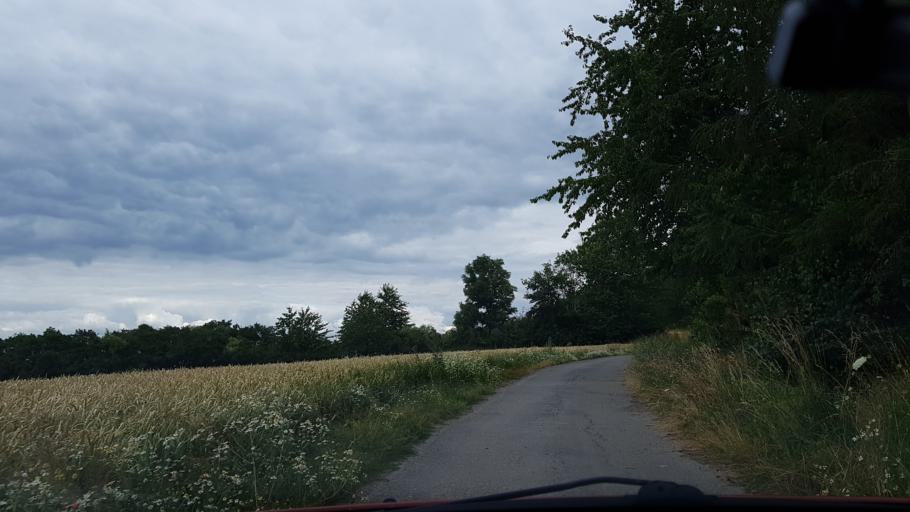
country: PL
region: Lower Silesian Voivodeship
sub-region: Powiat zabkowicki
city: Stoszowice
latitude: 50.5677
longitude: 16.7523
